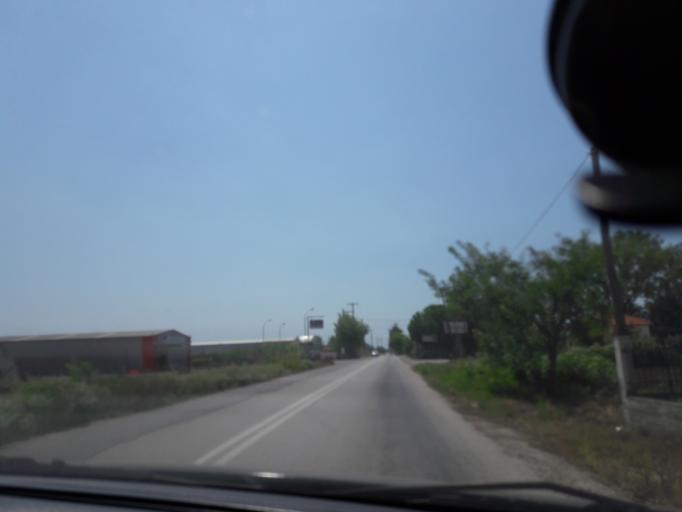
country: GR
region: Central Macedonia
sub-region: Nomos Chalkidikis
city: Nea Kallikrateia
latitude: 40.3368
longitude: 23.0642
